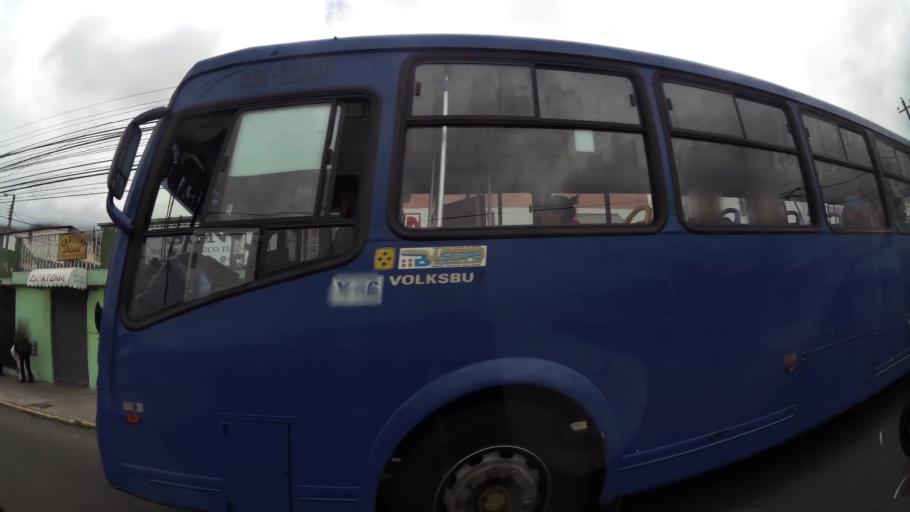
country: EC
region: Pichincha
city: Quito
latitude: -0.1243
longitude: -78.4987
